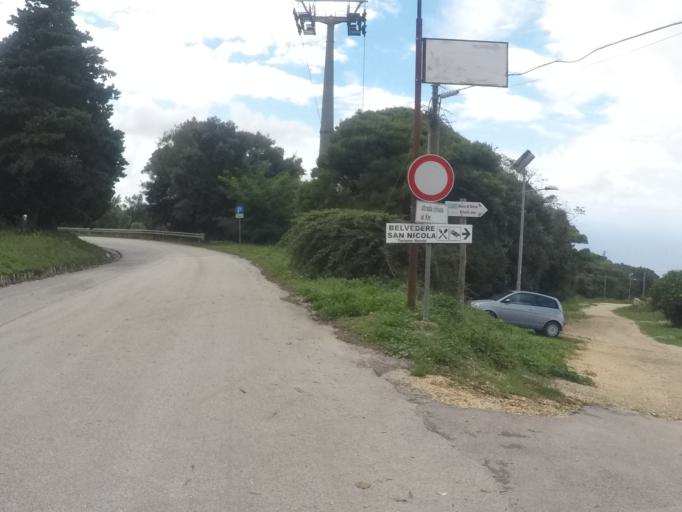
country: IT
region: Sicily
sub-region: Trapani
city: Erice
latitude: 38.0359
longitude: 12.5810
